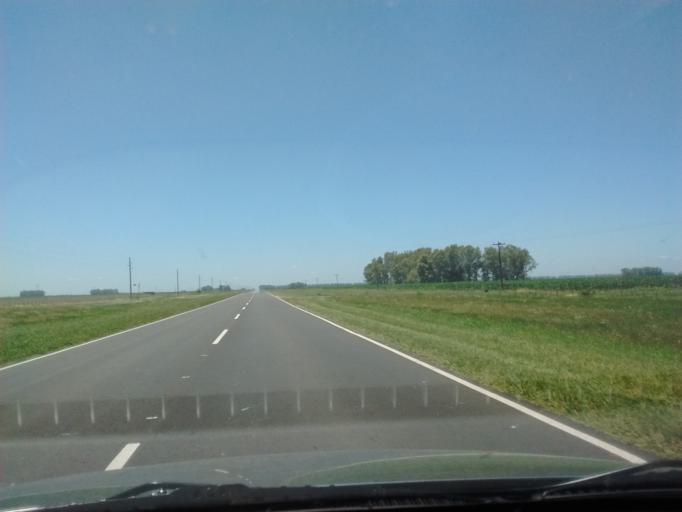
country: AR
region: Entre Rios
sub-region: Departamento de Gualeguay
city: Gualeguay
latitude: -32.9779
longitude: -59.5540
